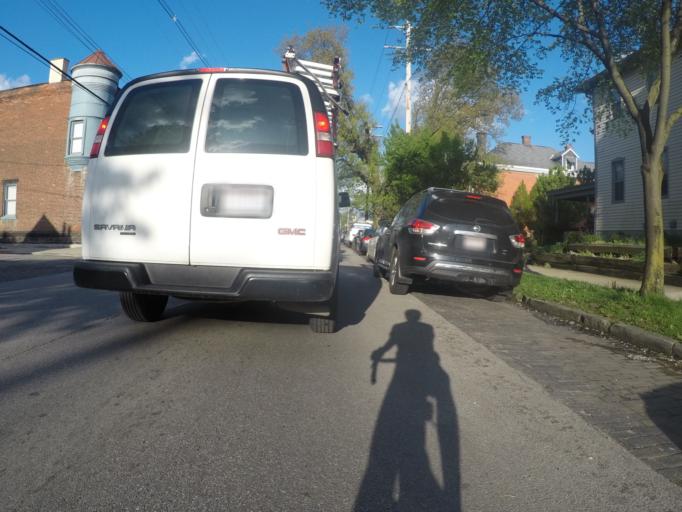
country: US
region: Ohio
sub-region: Franklin County
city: Columbus
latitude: 39.9445
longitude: -82.9915
